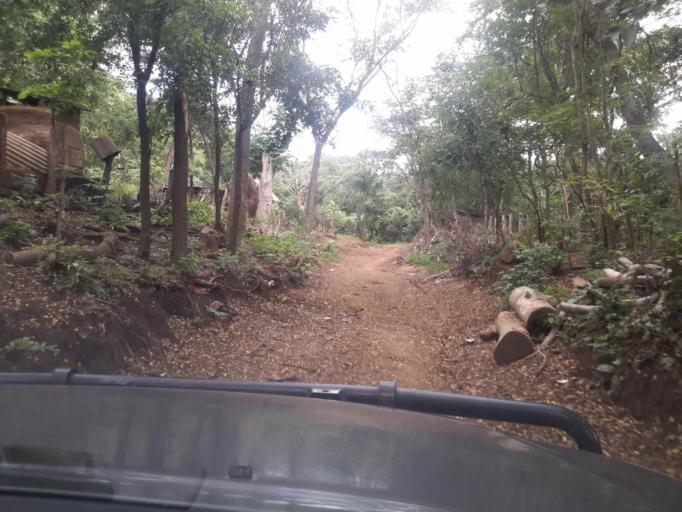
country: NI
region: Carazo
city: Santa Teresa
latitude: 11.6782
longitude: -86.3007
